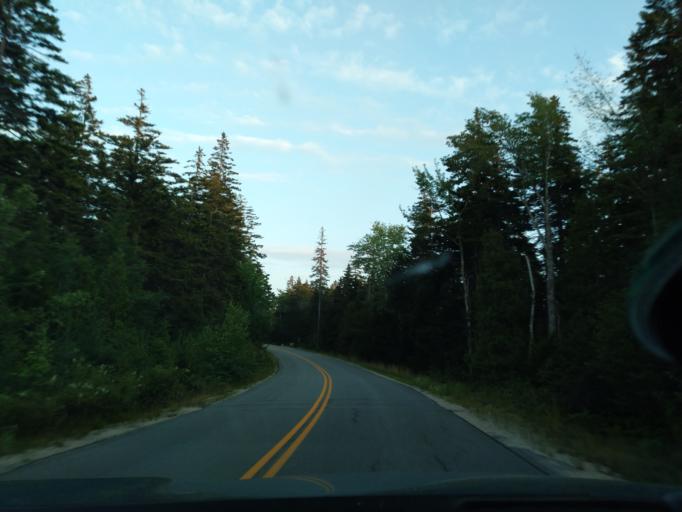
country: US
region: Maine
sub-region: Hancock County
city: Gouldsboro
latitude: 44.3902
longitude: -68.0728
